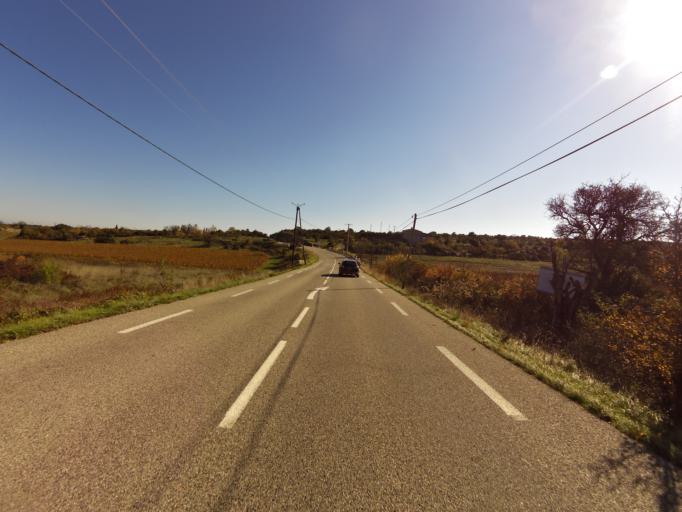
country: FR
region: Languedoc-Roussillon
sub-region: Departement du Gard
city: Saint-Julien-de-Peyrolas
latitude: 44.3858
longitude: 4.5166
